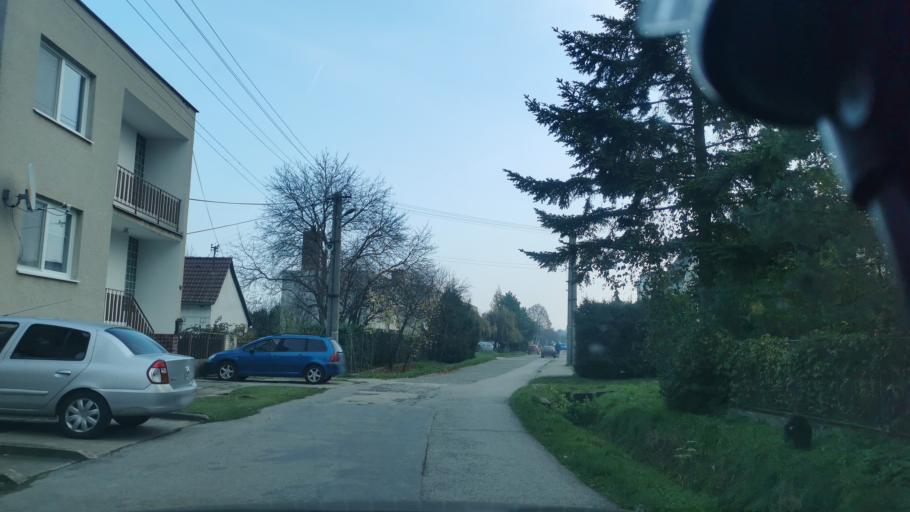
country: SK
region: Trnavsky
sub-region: Okres Skalica
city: Skalica
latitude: 48.7672
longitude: 17.2802
